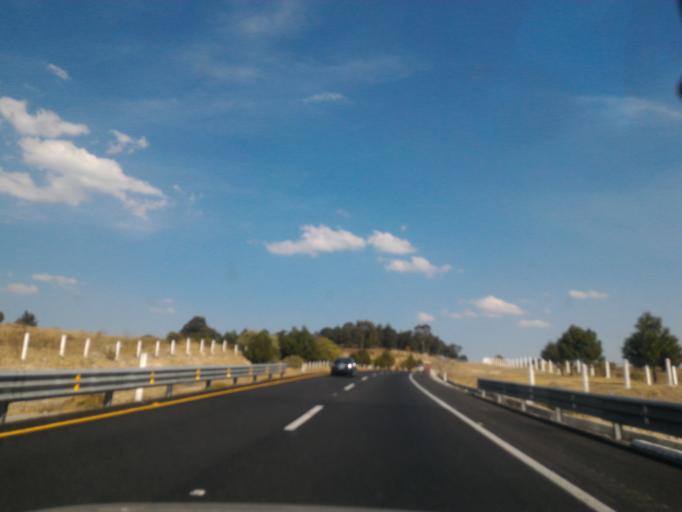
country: MX
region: Mexico
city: Temascalcingo de Jose Maria Velazco
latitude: 19.8545
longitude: -100.0090
